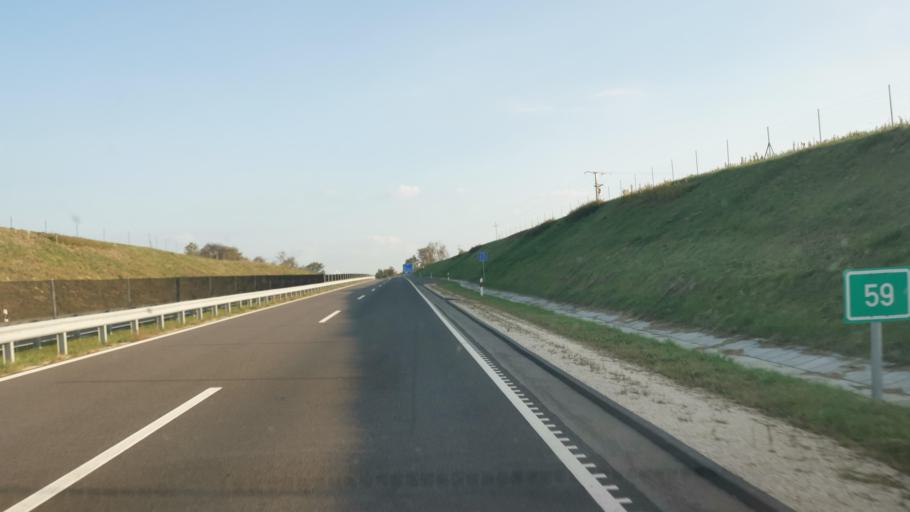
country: HU
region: Gyor-Moson-Sopron
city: Fertoszentmiklos
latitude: 47.5613
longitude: 16.8649
